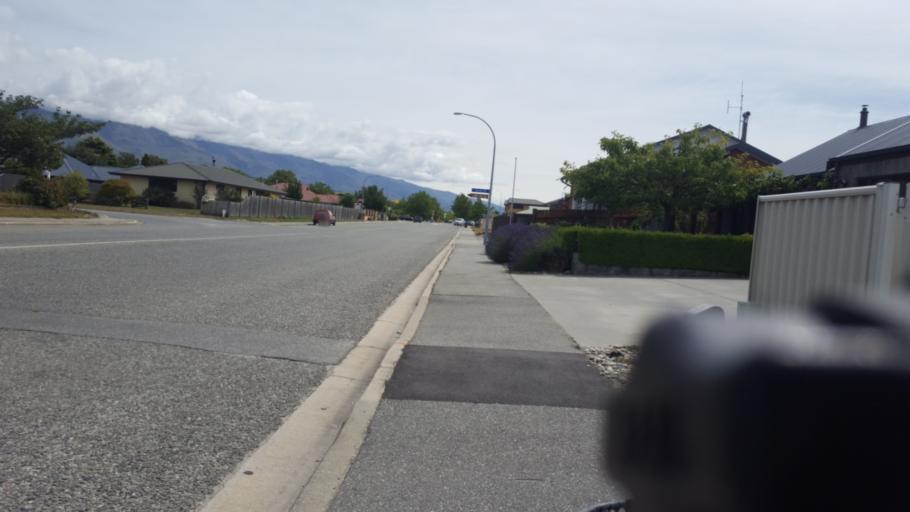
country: NZ
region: Otago
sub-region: Queenstown-Lakes District
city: Wanaka
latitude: -45.0475
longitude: 169.1951
